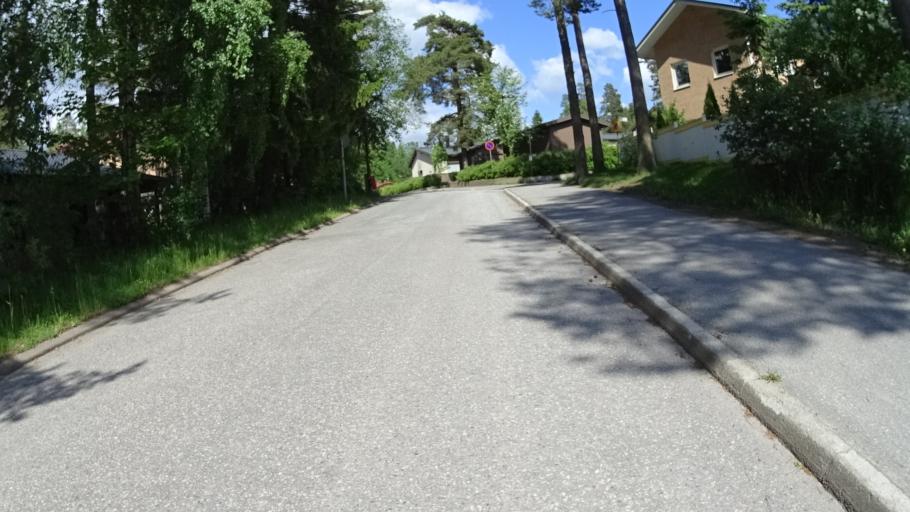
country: FI
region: Uusimaa
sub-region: Helsinki
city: Kauniainen
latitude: 60.1965
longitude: 24.7486
